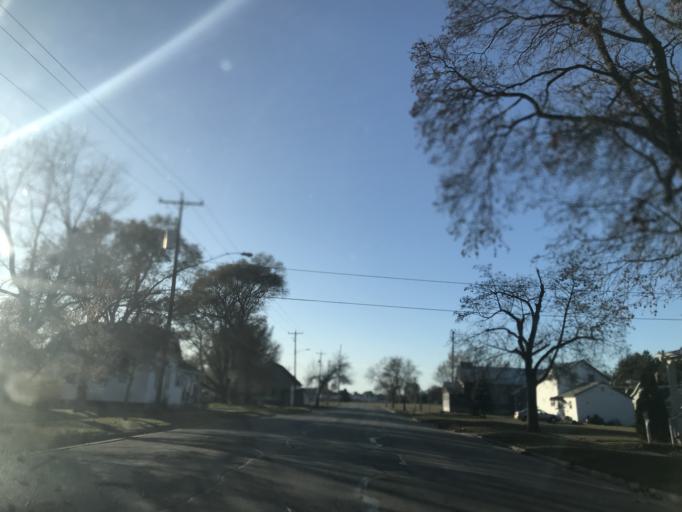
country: US
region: Wisconsin
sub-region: Marinette County
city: Peshtigo
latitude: 45.0550
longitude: -87.7423
